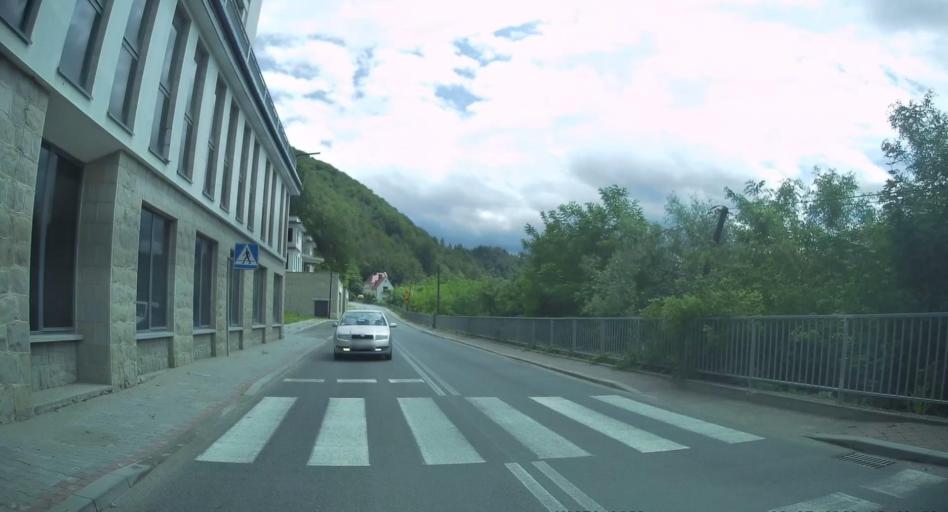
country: PL
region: Lesser Poland Voivodeship
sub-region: Powiat nowosadecki
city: Muszyna
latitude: 49.3594
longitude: 20.8103
